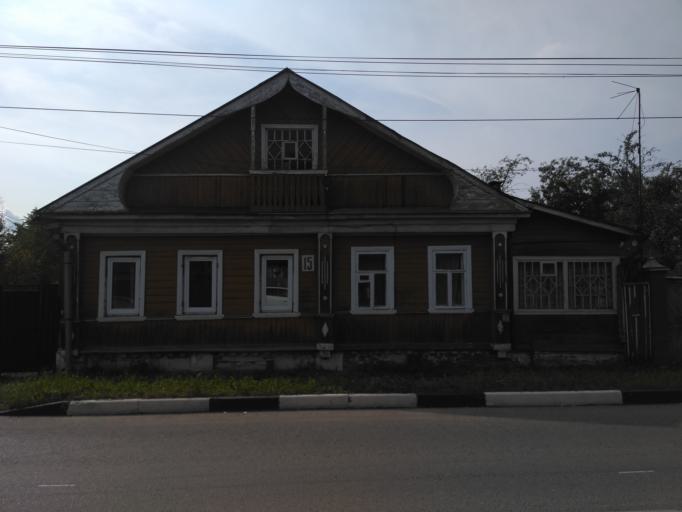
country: RU
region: Moskovskaya
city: Sergiyev Posad
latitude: 56.3147
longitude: 38.1251
